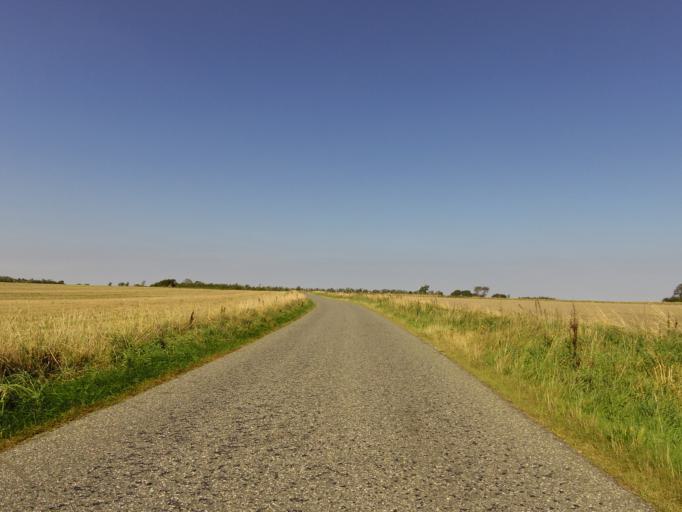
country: DK
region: South Denmark
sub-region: Haderslev Kommune
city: Gram
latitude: 55.3153
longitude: 9.1060
